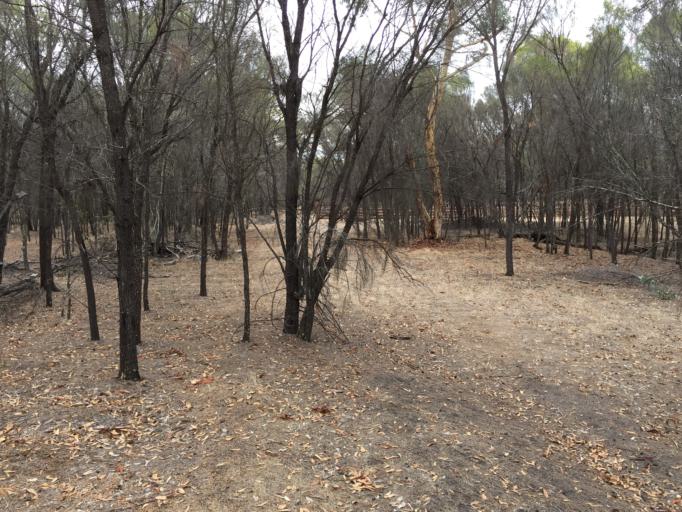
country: AU
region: Western Australia
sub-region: Narrogin
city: Narrogin
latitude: -32.8213
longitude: 116.8890
